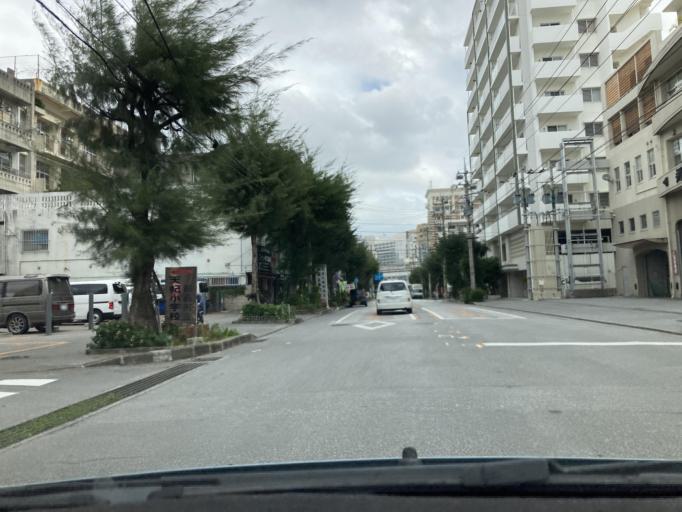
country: JP
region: Okinawa
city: Naha-shi
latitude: 26.2143
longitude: 127.6737
